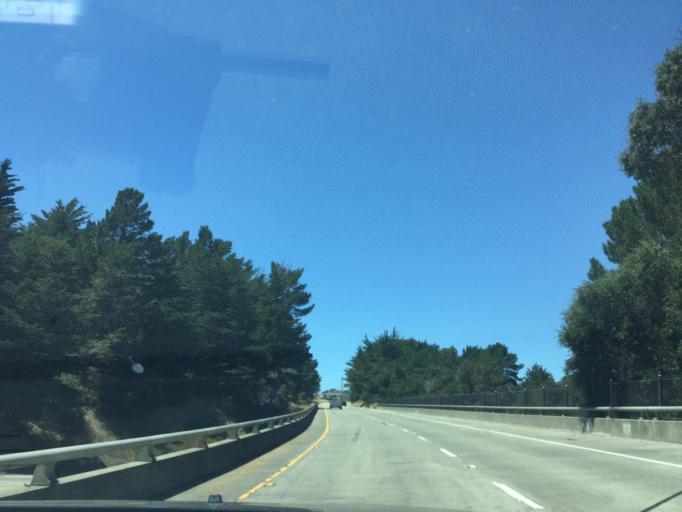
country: US
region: California
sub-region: San Mateo County
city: San Bruno
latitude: 37.6039
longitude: -122.4270
